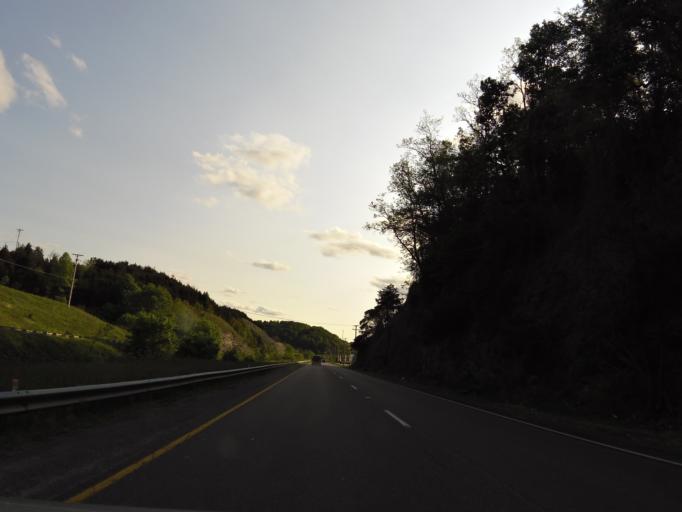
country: US
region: Virginia
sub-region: Tazewell County
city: Claypool Hill
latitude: 37.0470
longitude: -81.7812
